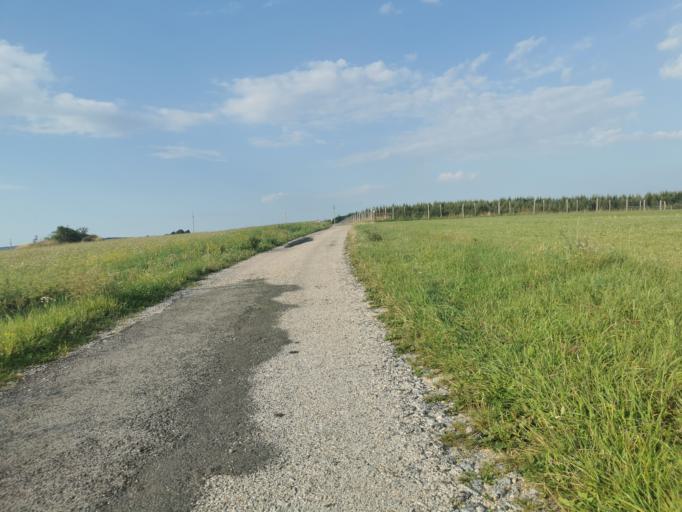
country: SK
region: Trenciansky
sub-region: Okres Myjava
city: Myjava
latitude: 48.7893
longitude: 17.5688
